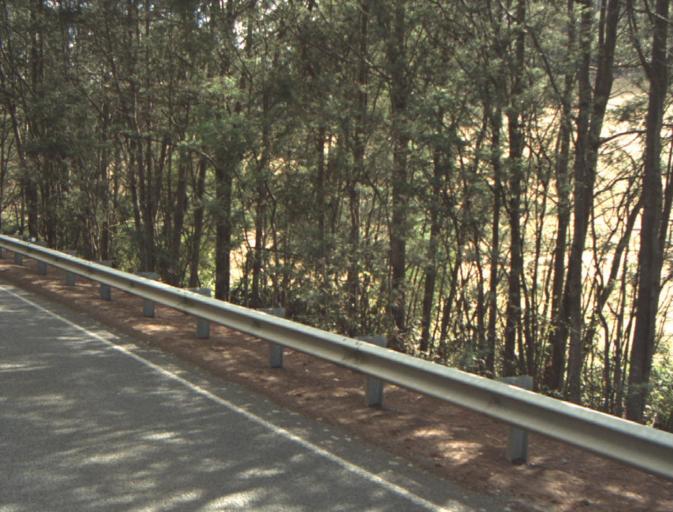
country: AU
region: Tasmania
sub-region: Launceston
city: Mayfield
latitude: -41.2886
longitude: 147.2175
